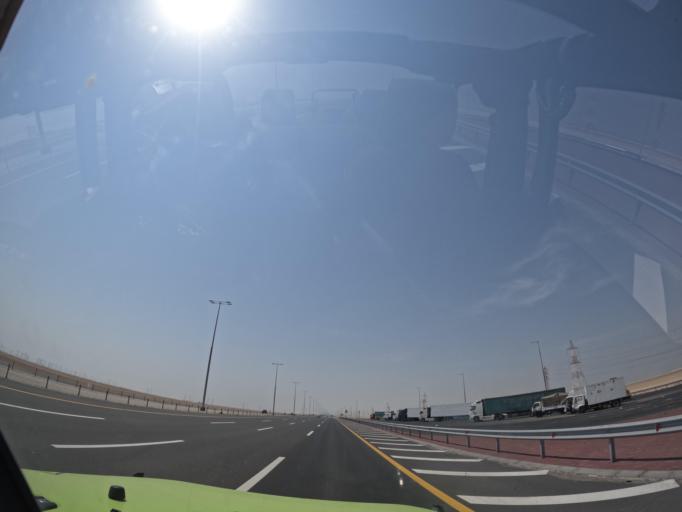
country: AE
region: Abu Dhabi
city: Abu Dhabi
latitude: 24.1568
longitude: 54.3281
